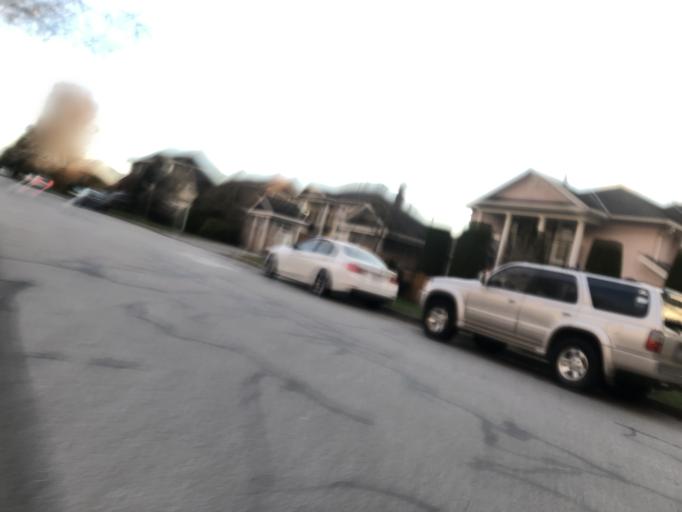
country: CA
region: British Columbia
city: Richmond
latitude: 49.1547
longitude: -123.1196
